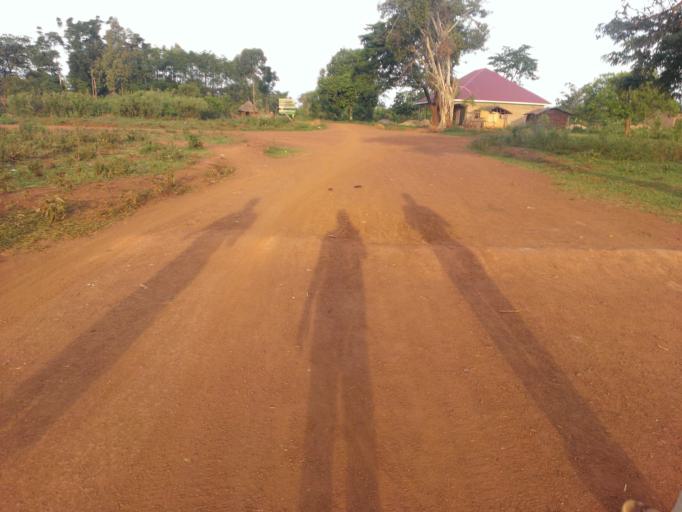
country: UG
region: Eastern Region
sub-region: Busia District
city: Busia
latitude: 0.5284
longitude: 34.0428
